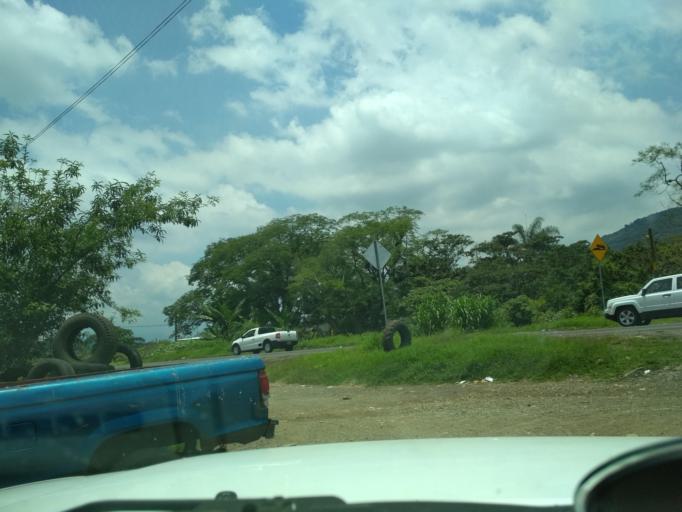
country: MX
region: Veracruz
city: Tocuila
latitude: 18.9506
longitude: -97.0175
